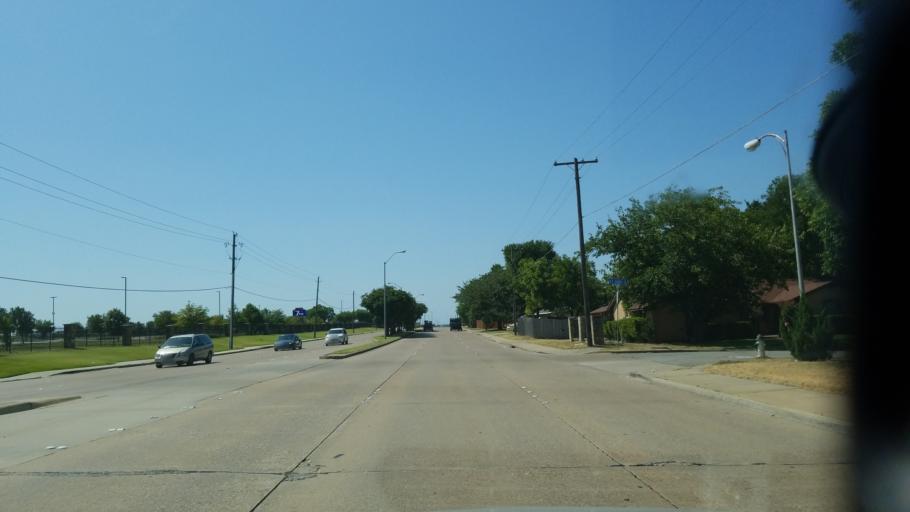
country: US
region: Texas
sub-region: Dallas County
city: Duncanville
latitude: 32.6531
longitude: -96.8914
